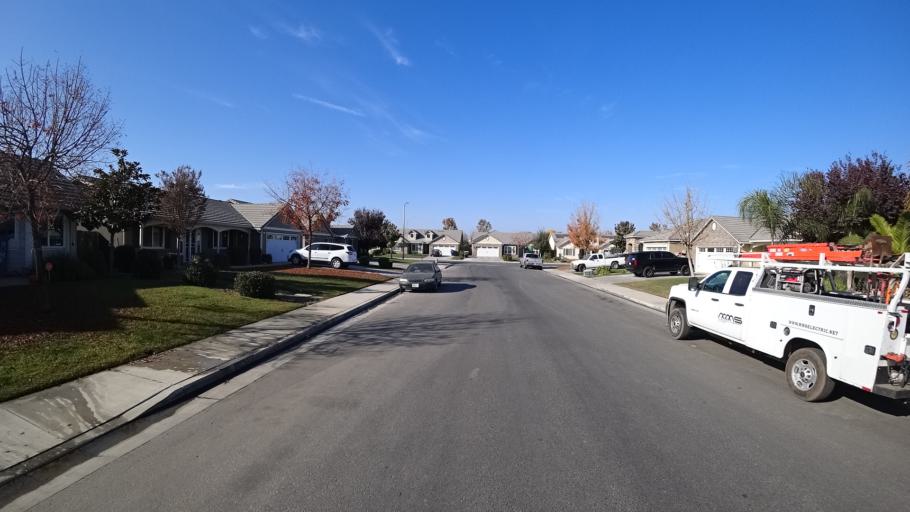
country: US
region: California
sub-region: Kern County
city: Greenfield
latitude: 35.2728
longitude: -119.0643
